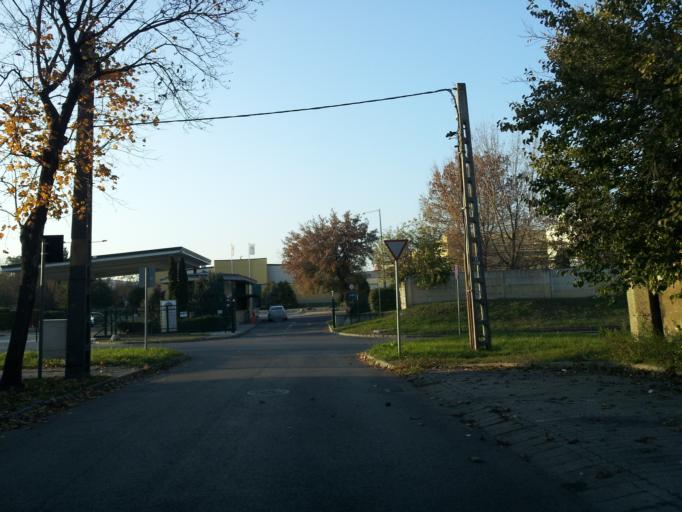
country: HU
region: Budapest
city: Budapest X. keruelet
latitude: 47.4855
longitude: 19.1493
